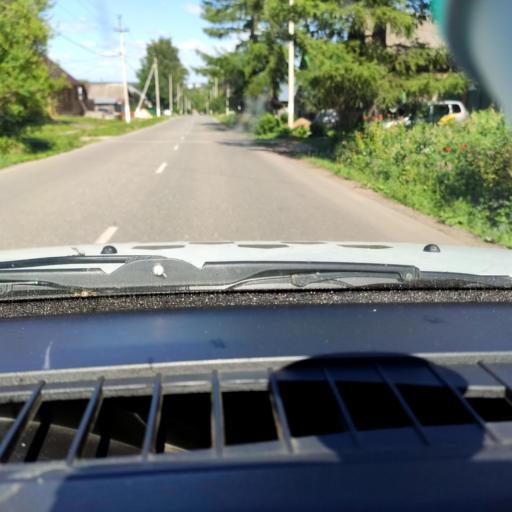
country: RU
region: Udmurtiya
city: Votkinsk
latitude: 57.0438
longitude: 53.9595
